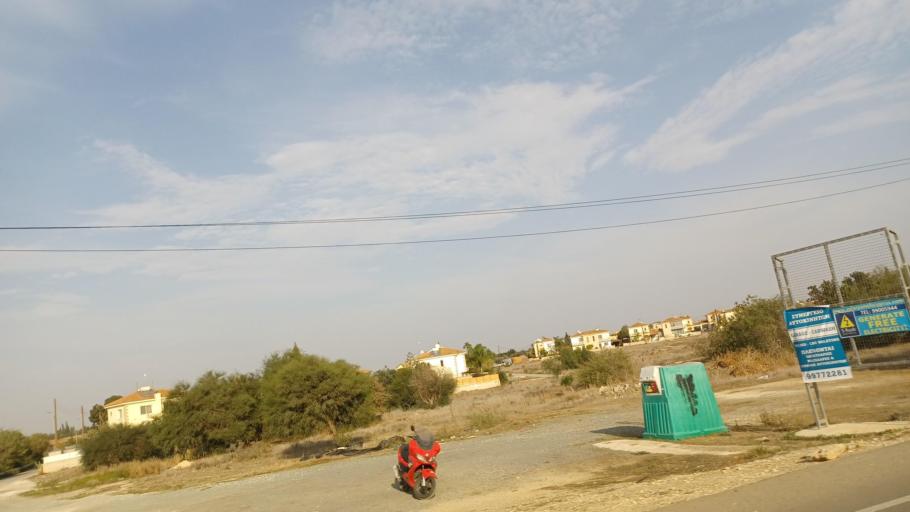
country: CY
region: Ammochostos
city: Frenaros
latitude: 35.0463
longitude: 33.9177
